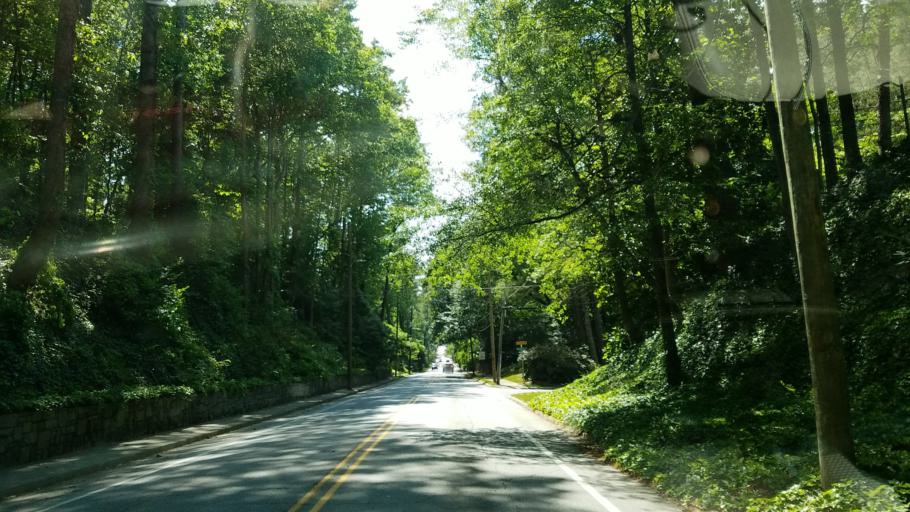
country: US
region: Georgia
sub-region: DeKalb County
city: North Atlanta
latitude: 33.8287
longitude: -84.3991
